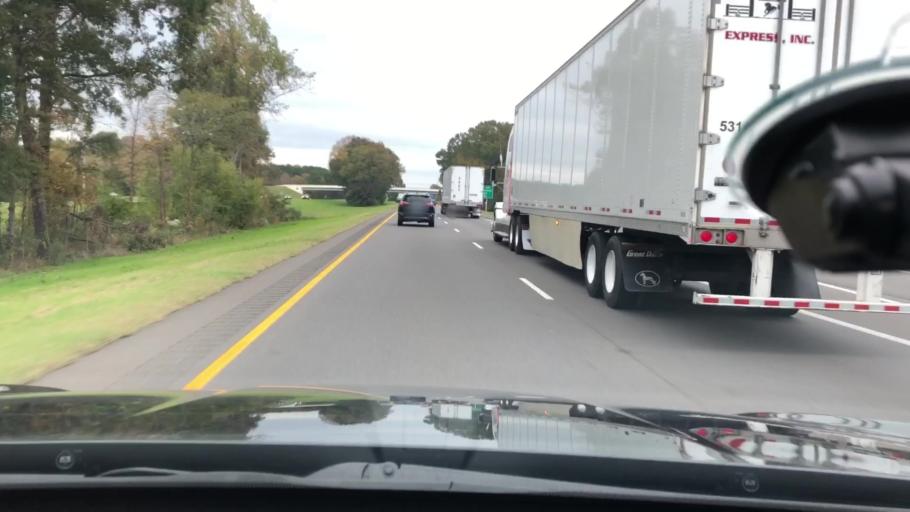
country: US
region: Arkansas
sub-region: Hempstead County
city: Hope
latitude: 33.6792
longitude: -93.6142
